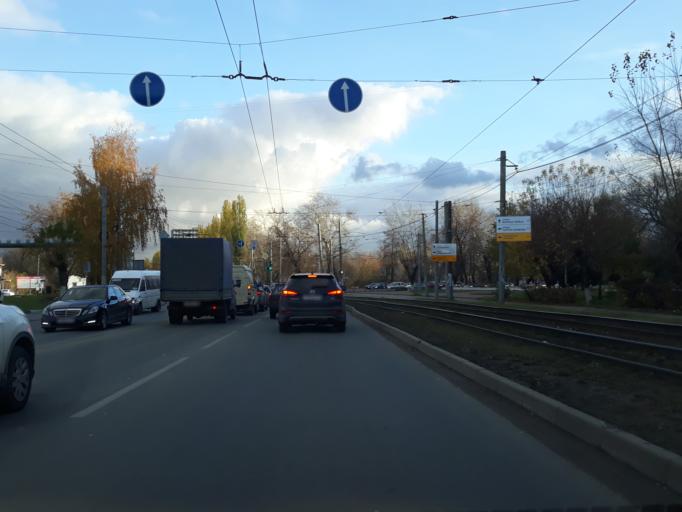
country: RU
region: Nizjnij Novgorod
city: Nizhniy Novgorod
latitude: 56.3369
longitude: 43.8850
